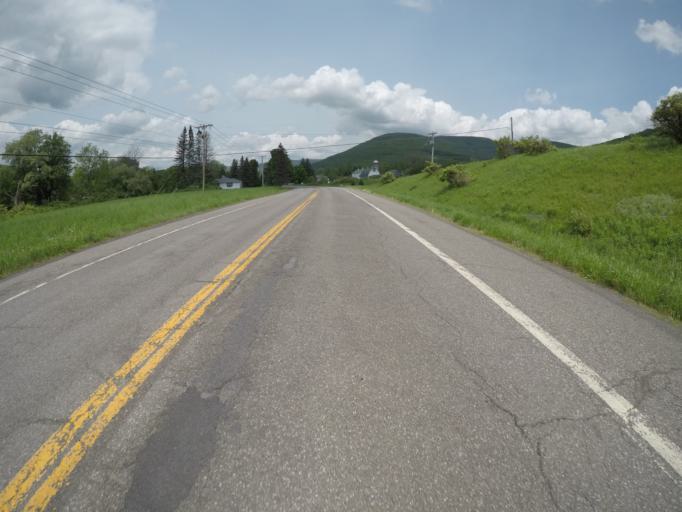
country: US
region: New York
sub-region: Delaware County
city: Stamford
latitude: 42.2775
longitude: -74.5699
